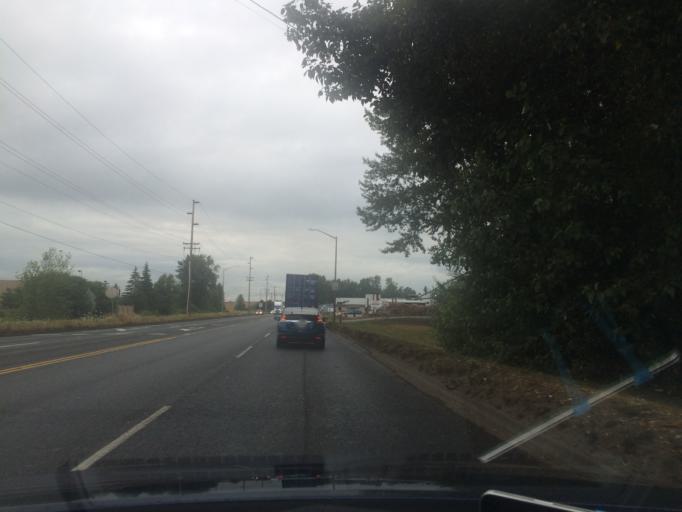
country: US
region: Washington
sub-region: Cowlitz County
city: Longview
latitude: 46.1173
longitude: -122.9292
